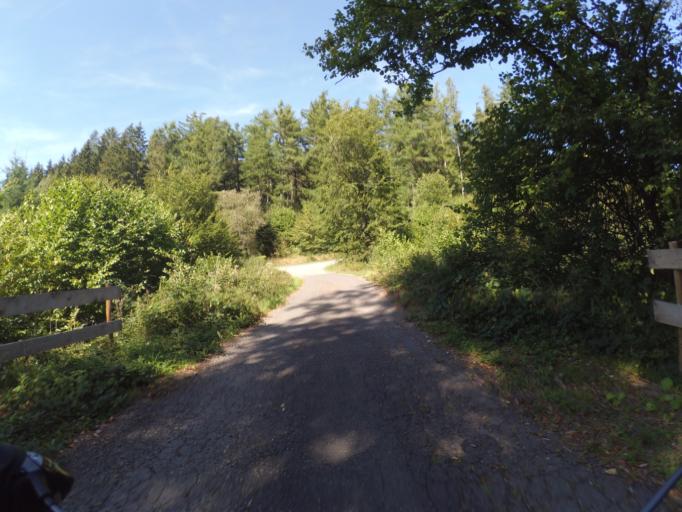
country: DE
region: Rheinland-Pfalz
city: Hilscheid
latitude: 49.7219
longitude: 7.0267
